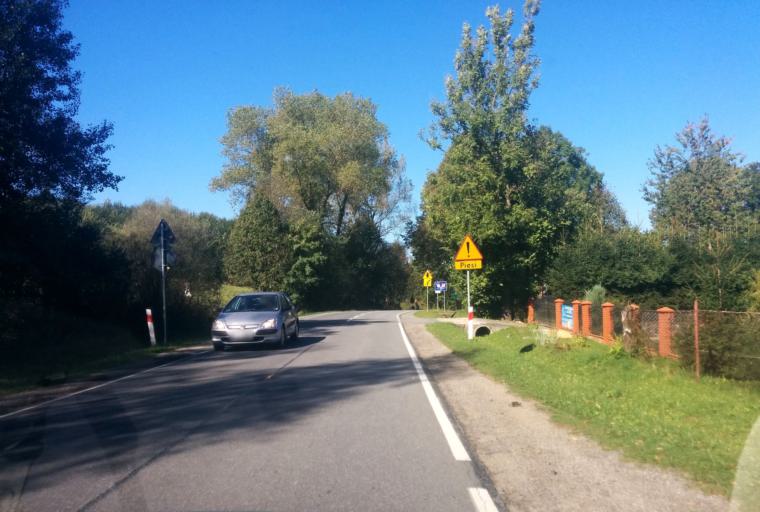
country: PL
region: Subcarpathian Voivodeship
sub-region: Powiat bieszczadzki
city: Czarna
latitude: 49.3209
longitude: 22.6702
